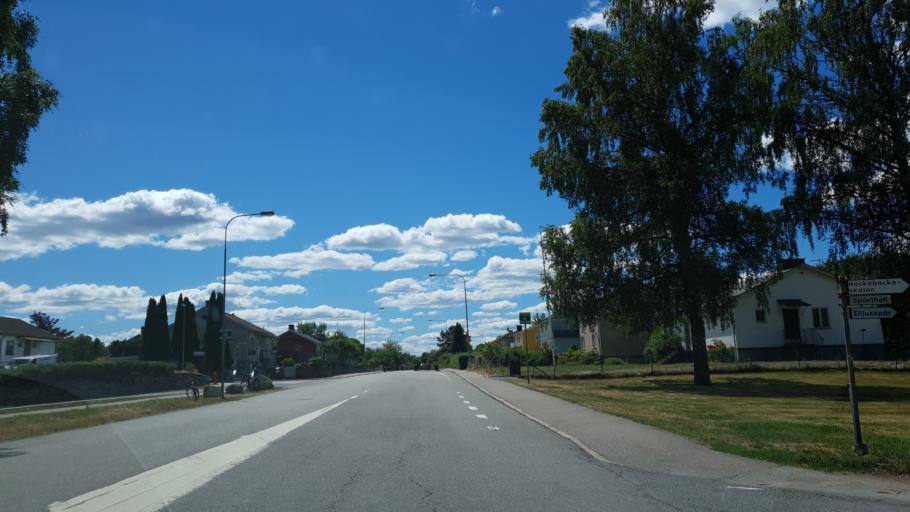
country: SE
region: Kronoberg
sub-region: Lessebo Kommun
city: Lessebo
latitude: 56.7541
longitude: 15.2817
